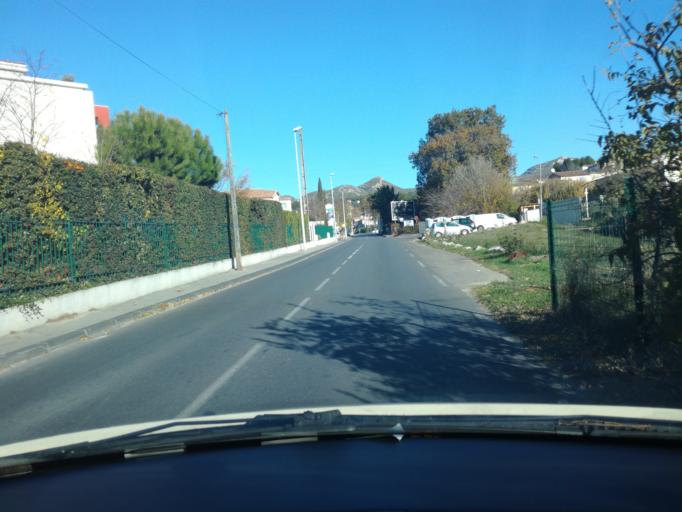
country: FR
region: Provence-Alpes-Cote d'Azur
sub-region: Departement des Bouches-du-Rhone
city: La Penne-sur-Huveaune
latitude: 43.3047
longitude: 5.5010
